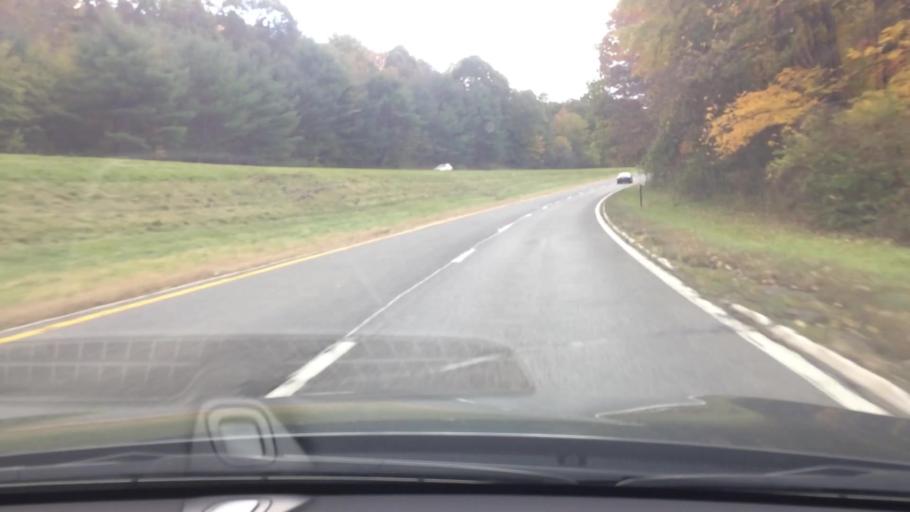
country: US
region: New York
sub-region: Dutchess County
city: Pine Plains
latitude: 41.9634
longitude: -73.7512
